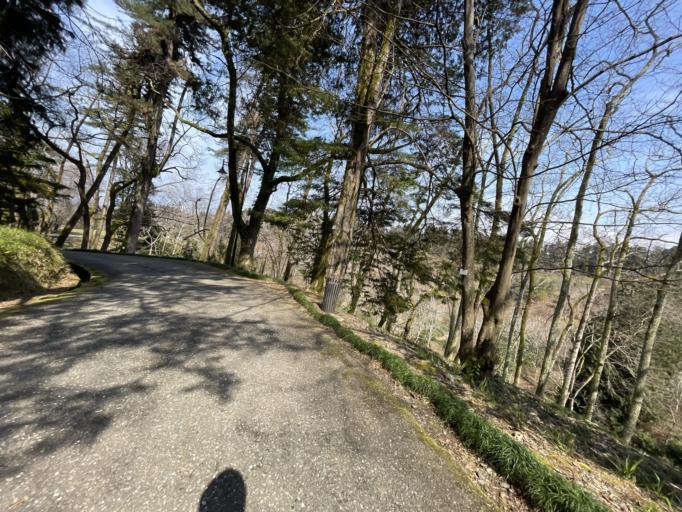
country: GE
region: Ajaria
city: Makhinjauri
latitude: 41.7038
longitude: 41.7217
